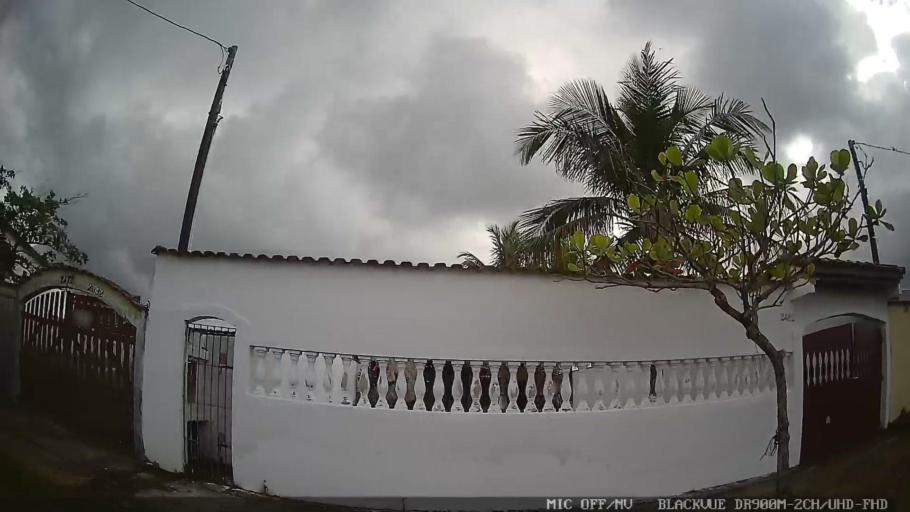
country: BR
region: Sao Paulo
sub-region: Itanhaem
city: Itanhaem
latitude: -24.2038
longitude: -46.8445
